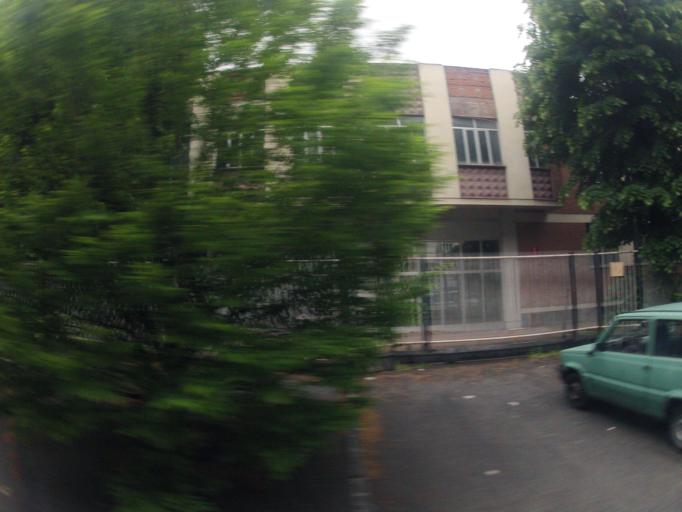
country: IT
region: Piedmont
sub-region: Provincia di Torino
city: Moncalieri
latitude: 45.0092
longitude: 7.6677
